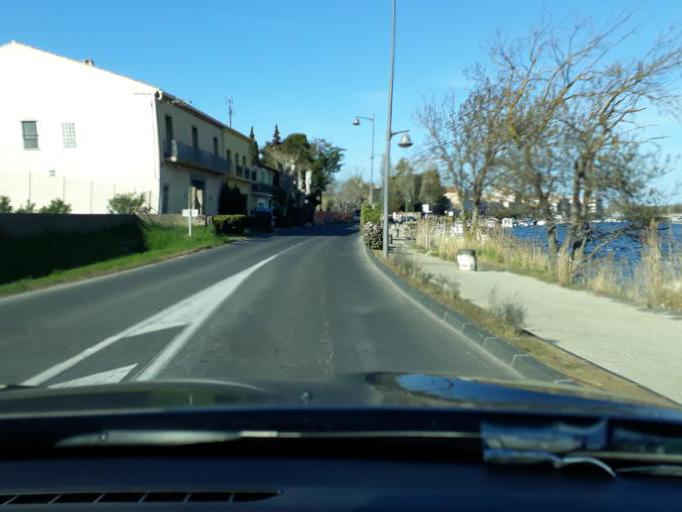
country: FR
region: Languedoc-Roussillon
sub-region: Departement de l'Herault
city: Agde
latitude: 43.3098
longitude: 3.4639
